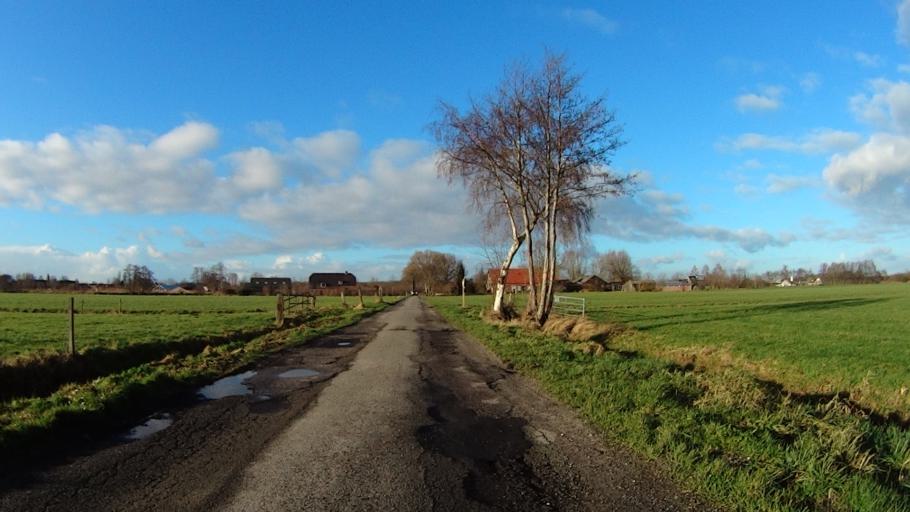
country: NL
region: Gelderland
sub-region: Gemeente Barneveld
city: Zwartebroek
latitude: 52.1768
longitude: 5.5153
